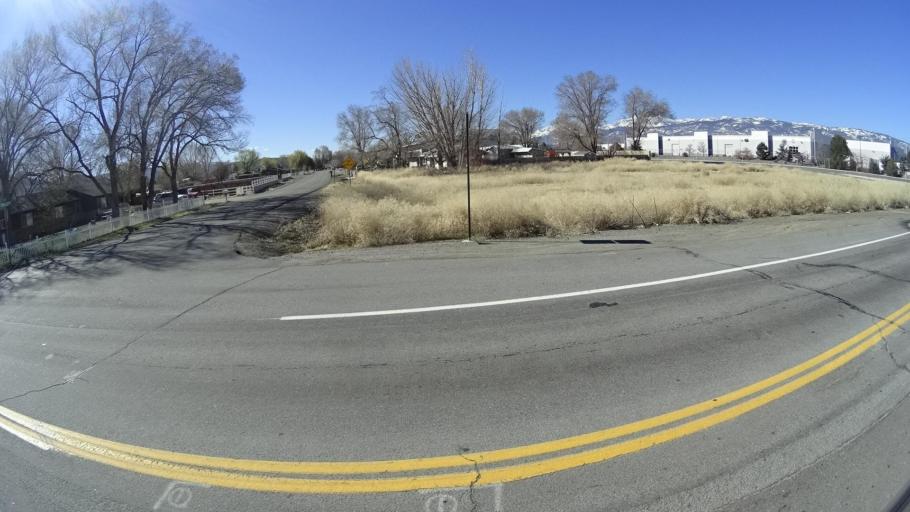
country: US
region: Nevada
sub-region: Washoe County
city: Sparks
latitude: 39.4976
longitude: -119.7471
